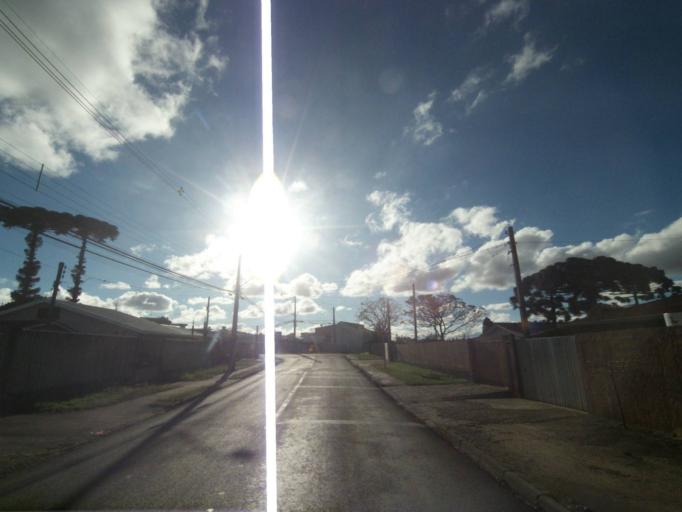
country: BR
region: Parana
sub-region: Sao Jose Dos Pinhais
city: Sao Jose dos Pinhais
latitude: -25.5286
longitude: -49.2836
